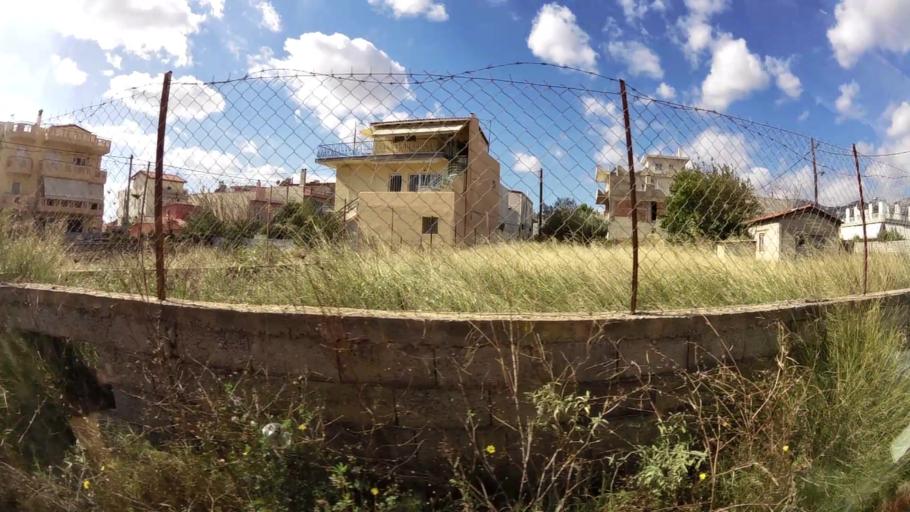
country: GR
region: Attica
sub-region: Nomarchia Anatolikis Attikis
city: Thrakomakedones
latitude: 38.1058
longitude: 23.7497
